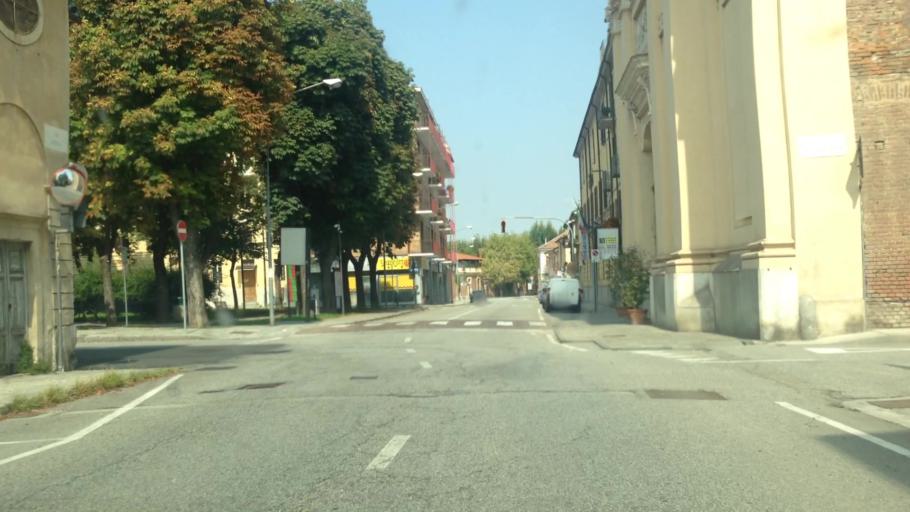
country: IT
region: Piedmont
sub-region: Provincia di Alessandria
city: Casale Monferrato
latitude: 45.1375
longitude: 8.4566
